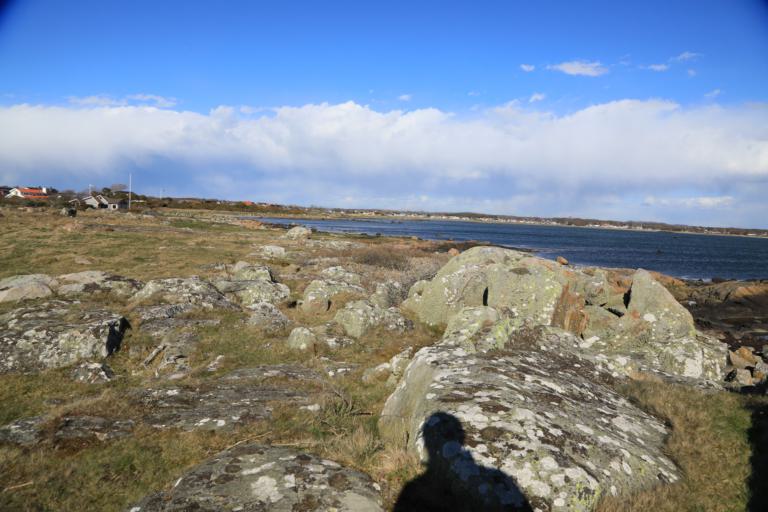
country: SE
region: Halland
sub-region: Varbergs Kommun
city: Traslovslage
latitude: 57.0645
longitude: 12.2563
